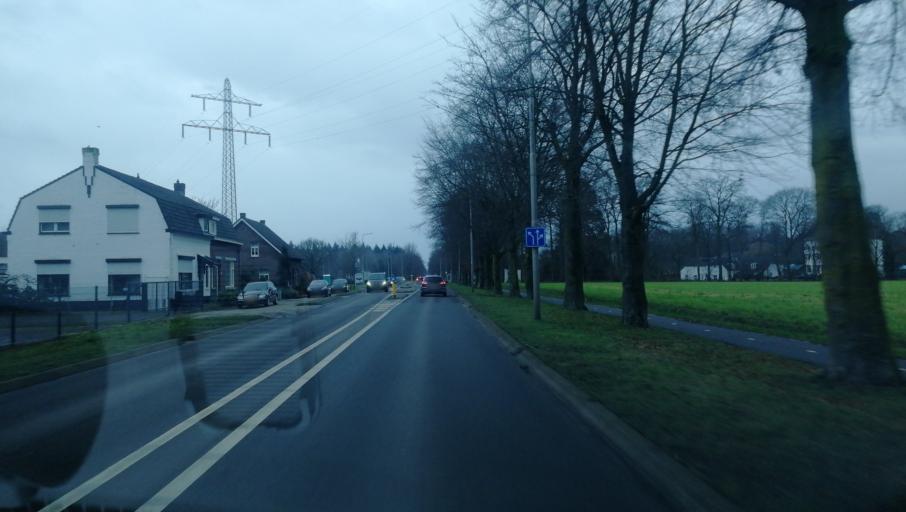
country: NL
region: Limburg
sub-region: Gemeente Beesel
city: Reuver
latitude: 51.3263
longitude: 6.0858
